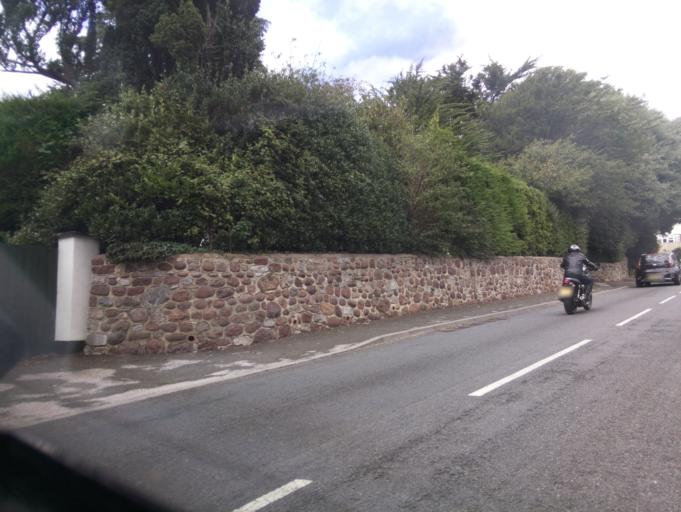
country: GB
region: England
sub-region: Devon
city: Teignmouth
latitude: 50.5549
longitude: -3.4910
